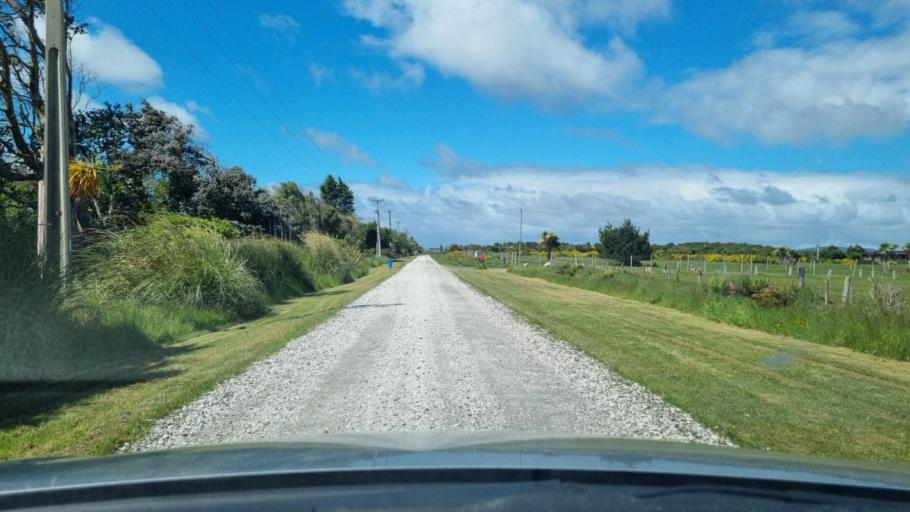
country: NZ
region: Southland
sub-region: Invercargill City
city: Invercargill
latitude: -46.4487
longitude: 168.3166
